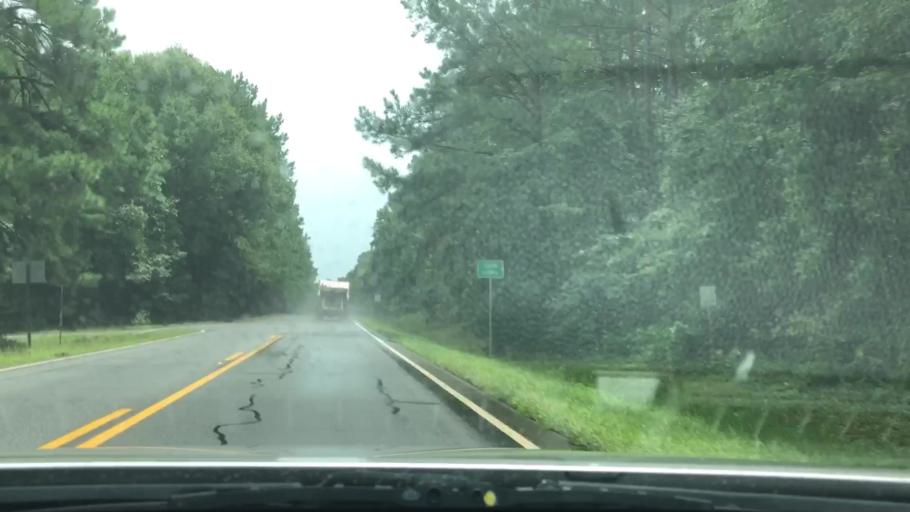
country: US
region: Georgia
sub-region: Lamar County
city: Barnesville
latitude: 33.0757
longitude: -84.2488
